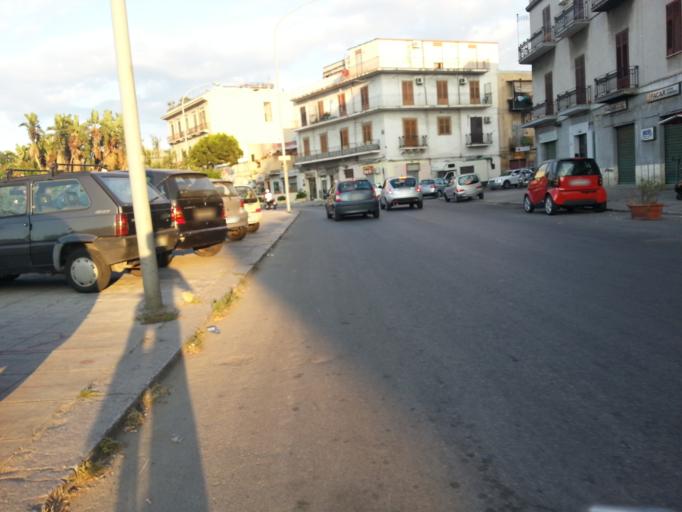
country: IT
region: Sicily
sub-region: Palermo
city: Ciaculli
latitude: 38.1049
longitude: 13.3742
